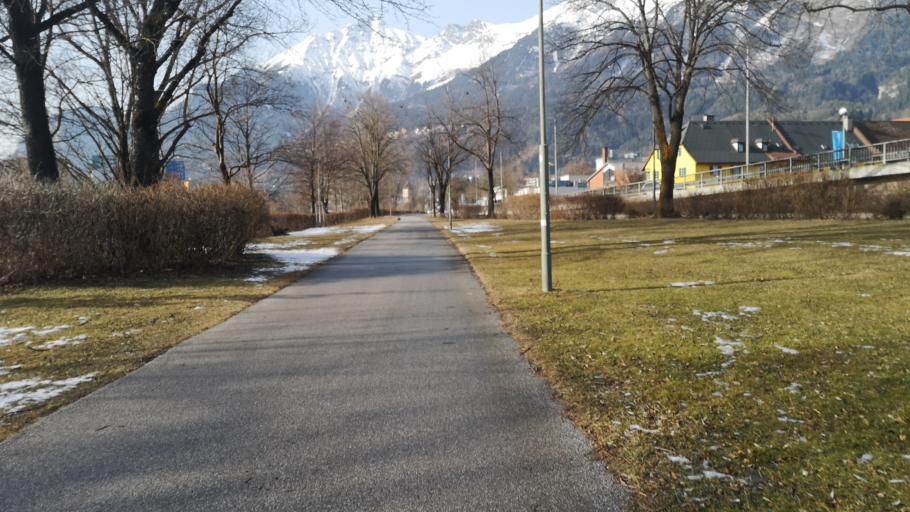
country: AT
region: Tyrol
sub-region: Politischer Bezirk Innsbruck Land
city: Ampass
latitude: 47.2750
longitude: 11.4299
